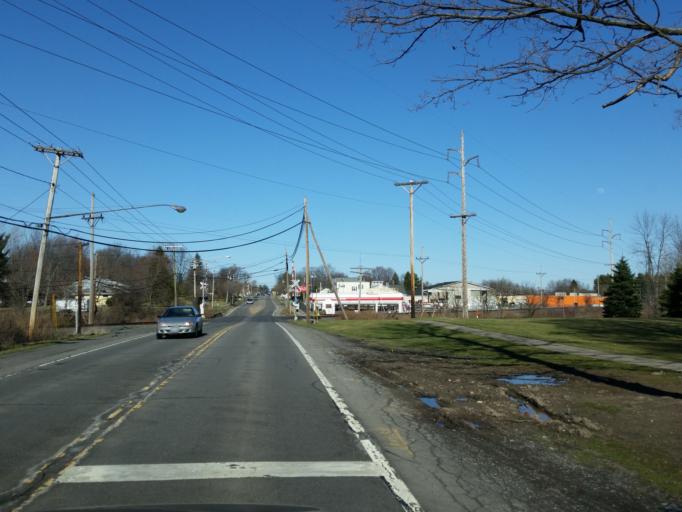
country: US
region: New York
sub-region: Monroe County
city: Scottsville
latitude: 43.1004
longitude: -77.7598
